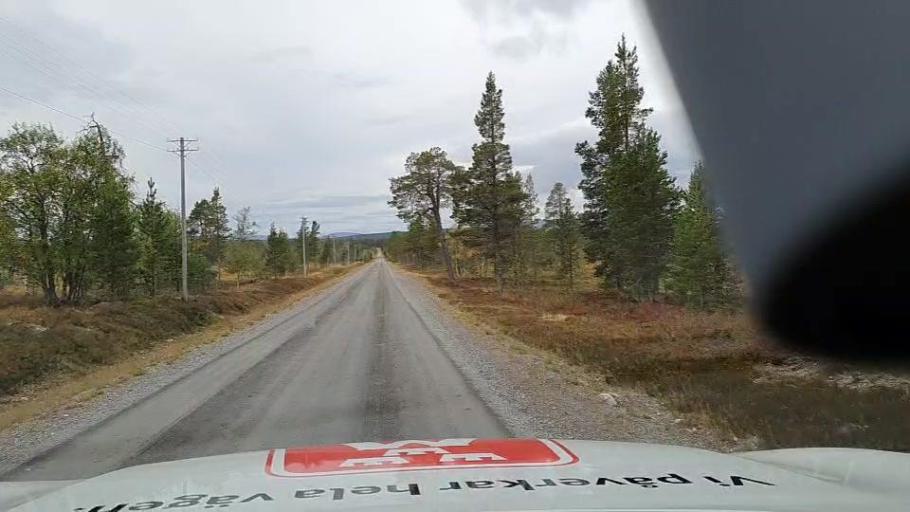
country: NO
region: Hedmark
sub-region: Engerdal
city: Engerdal
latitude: 62.0933
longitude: 12.8062
